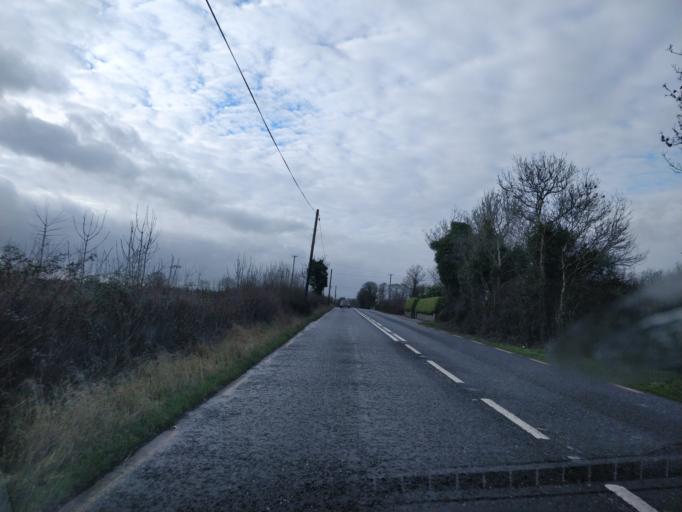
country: IE
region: Connaught
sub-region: Roscommon
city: Roscommon
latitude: 53.7686
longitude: -8.1602
